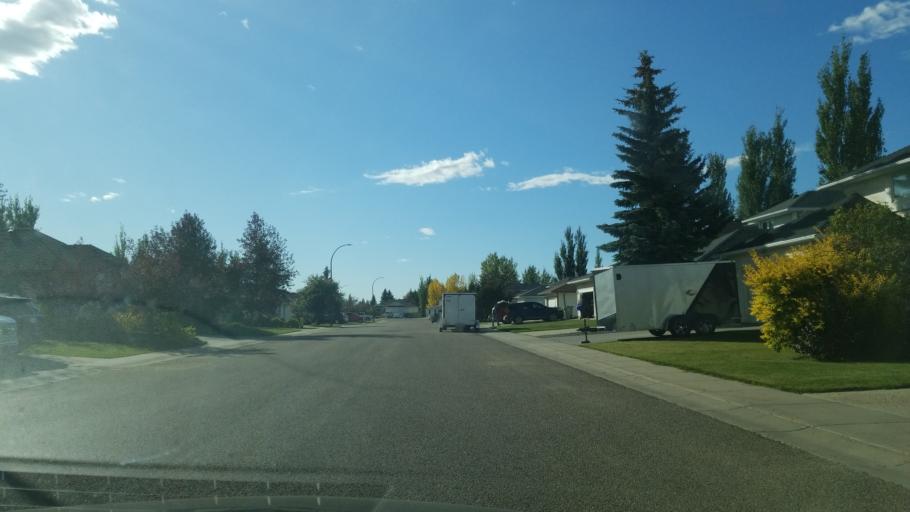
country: CA
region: Saskatchewan
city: Lloydminster
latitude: 53.2589
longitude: -110.0197
